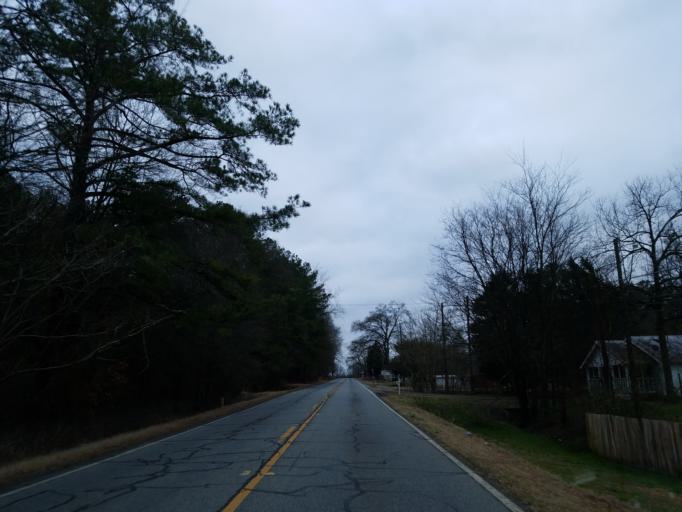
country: US
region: Georgia
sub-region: Bartow County
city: Cartersville
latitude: 34.1958
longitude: -84.8242
